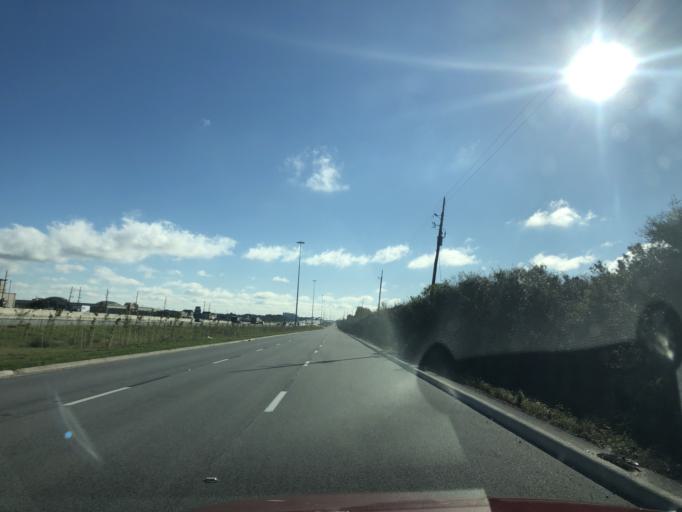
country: US
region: Texas
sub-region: Harris County
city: Cypress
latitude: 29.9942
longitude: -95.7578
